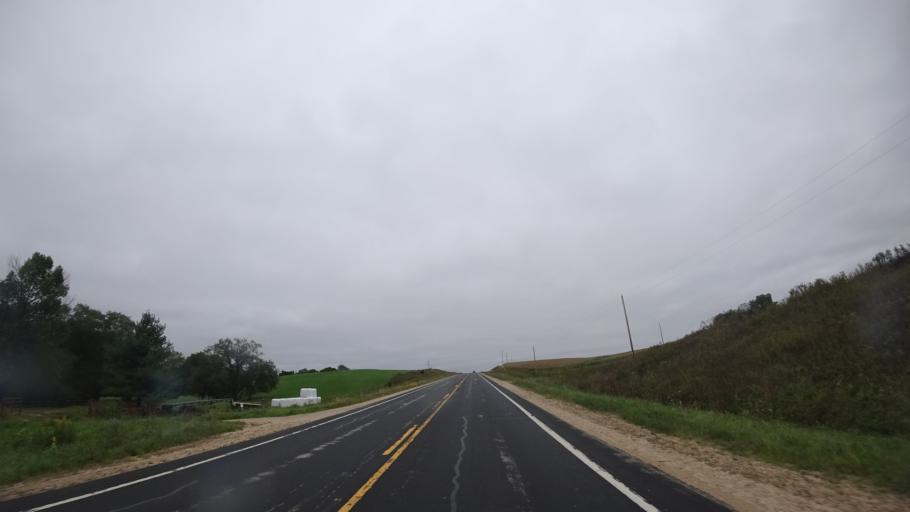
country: US
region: Wisconsin
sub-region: Grant County
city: Boscobel
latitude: 43.1082
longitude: -90.8074
